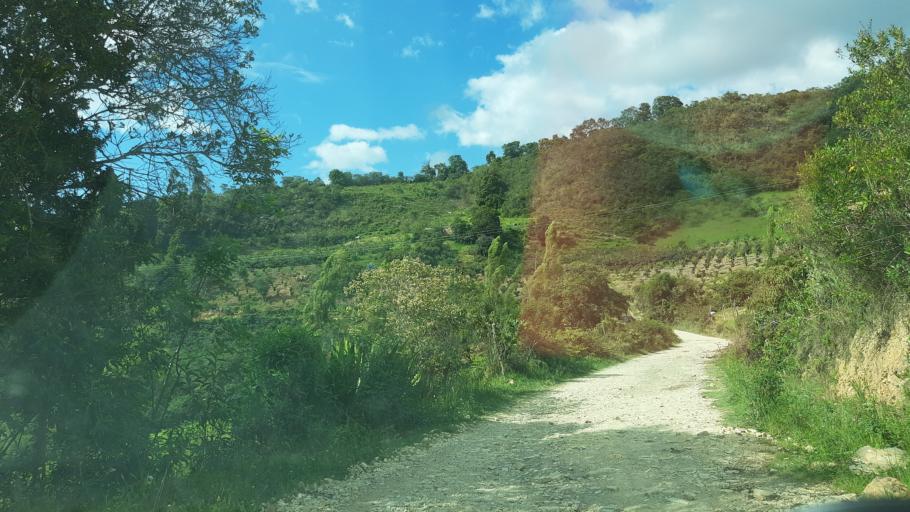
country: CO
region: Boyaca
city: Santa Sofia
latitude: 5.7309
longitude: -73.5526
